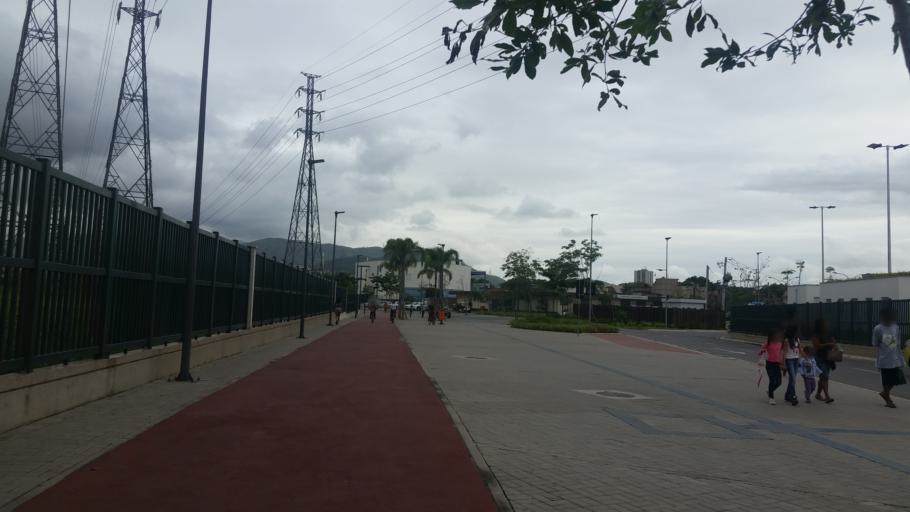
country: BR
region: Rio de Janeiro
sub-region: Sao Joao De Meriti
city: Sao Joao de Meriti
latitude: -22.8599
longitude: -43.3475
